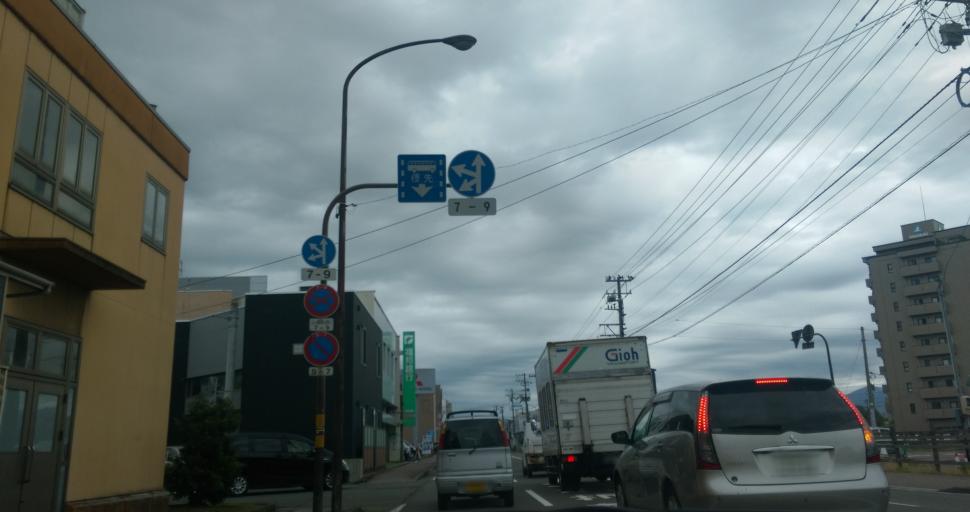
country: JP
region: Fukui
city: Fukui-shi
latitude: 36.0780
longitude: 136.2199
